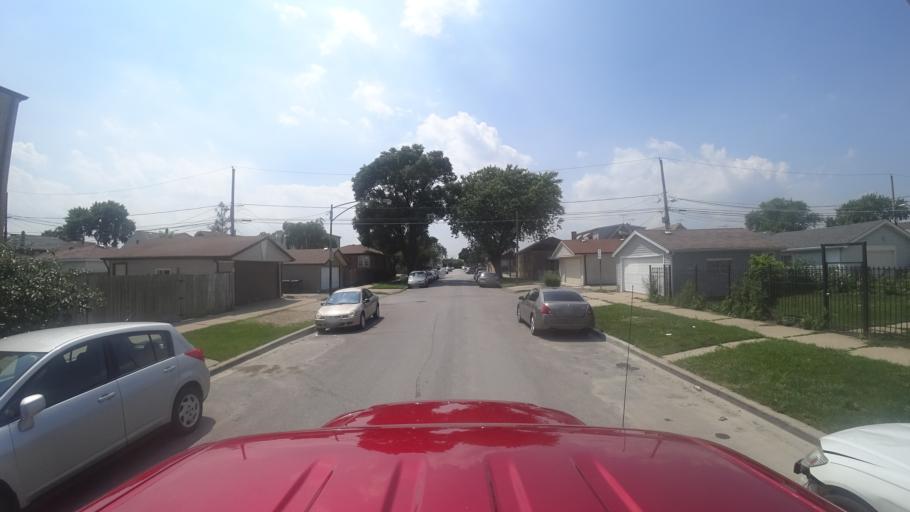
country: US
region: Illinois
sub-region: Cook County
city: Cicero
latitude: 41.7986
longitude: -87.7334
